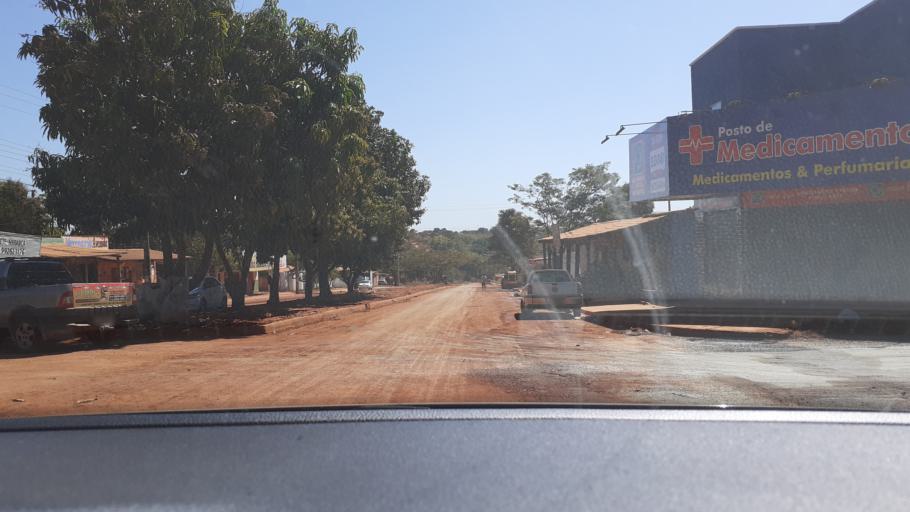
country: BR
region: Goias
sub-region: Aparecida De Goiania
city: Aparecida de Goiania
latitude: -16.8779
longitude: -49.2566
